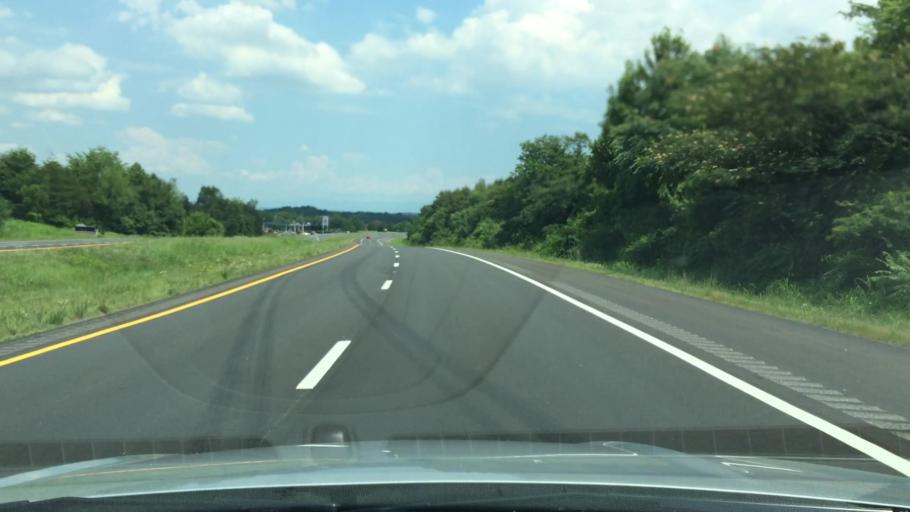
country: US
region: Tennessee
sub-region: Hamblen County
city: Morristown
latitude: 36.1705
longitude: -83.2265
